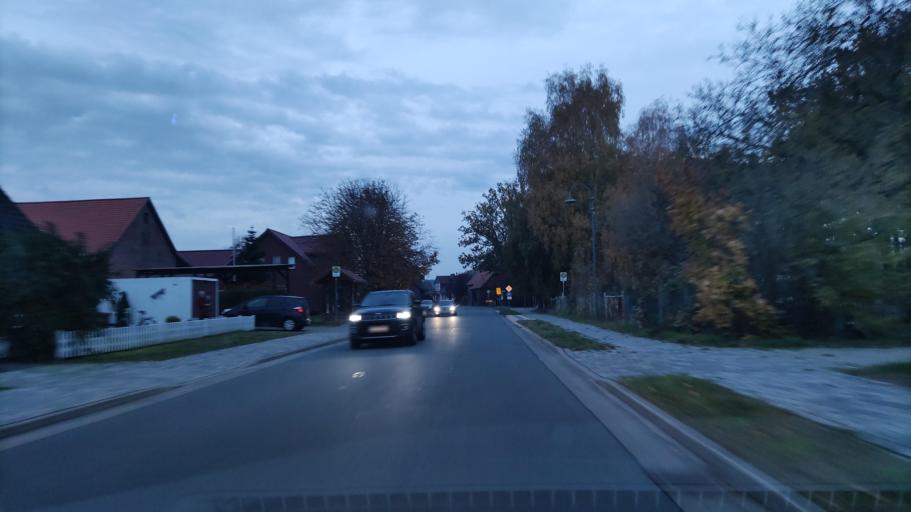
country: DE
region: Lower Saxony
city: Bergfeld
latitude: 52.5457
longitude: 10.8513
